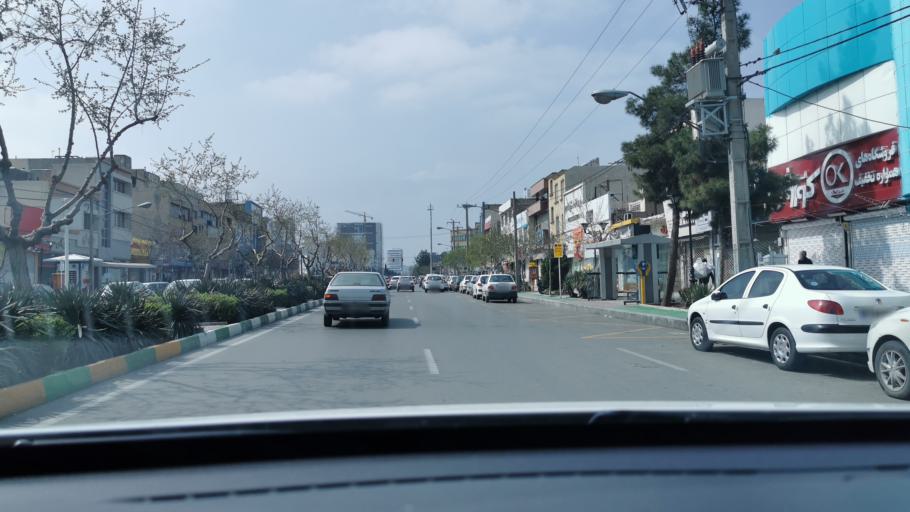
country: IR
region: Razavi Khorasan
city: Mashhad
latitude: 36.3274
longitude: 59.5369
